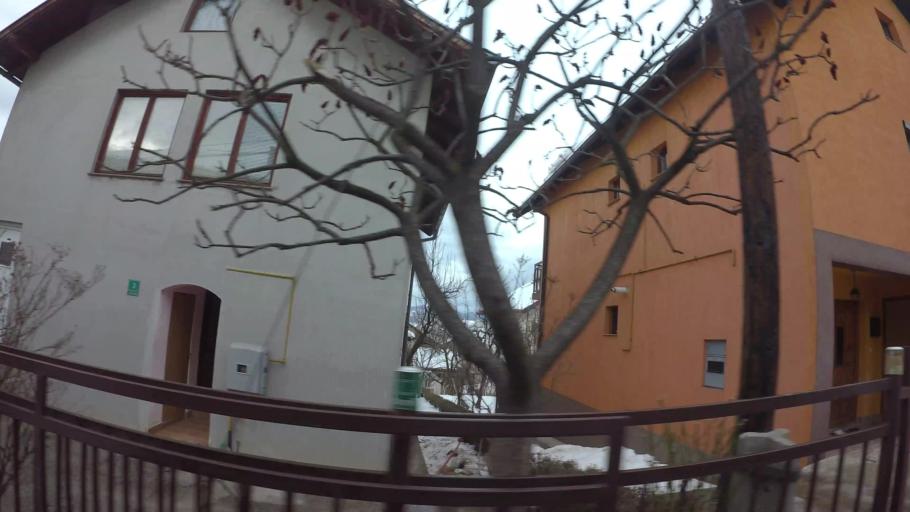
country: BA
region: Federation of Bosnia and Herzegovina
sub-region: Kanton Sarajevo
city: Sarajevo
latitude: 43.8681
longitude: 18.3204
